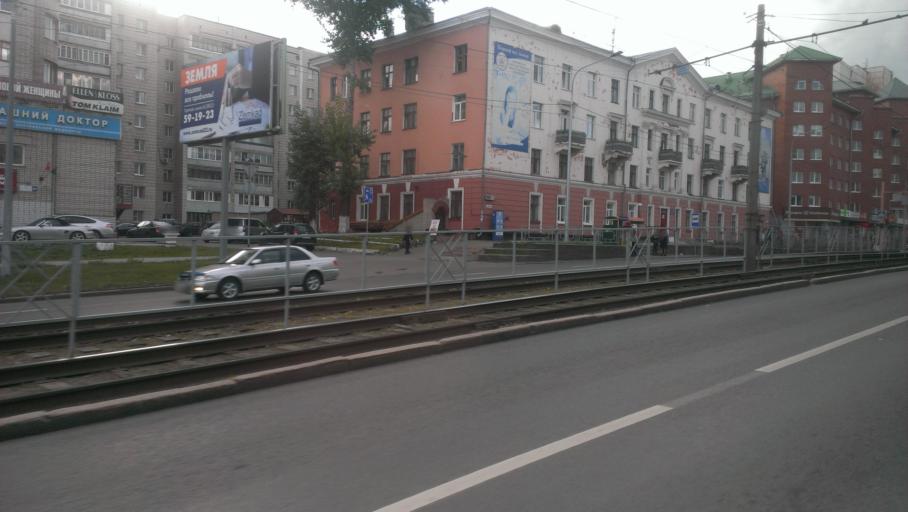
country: RU
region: Altai Krai
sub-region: Gorod Barnaulskiy
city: Barnaul
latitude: 53.3418
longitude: 83.7700
